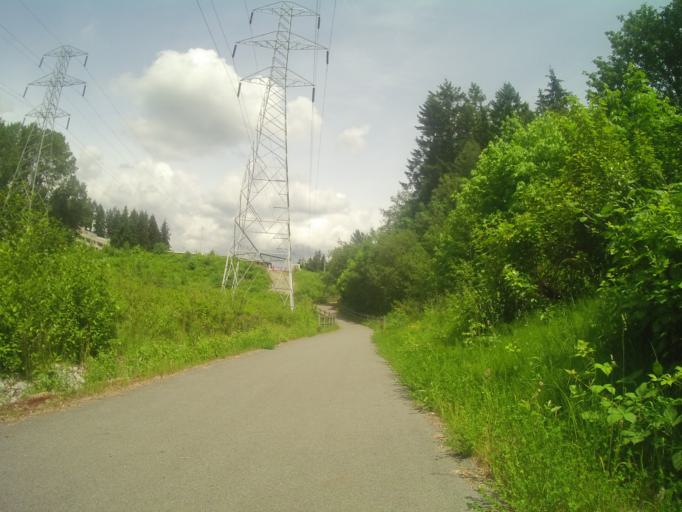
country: CA
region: British Columbia
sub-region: Fraser Valley Regional District
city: North Vancouver
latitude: 49.3139
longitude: -123.0207
